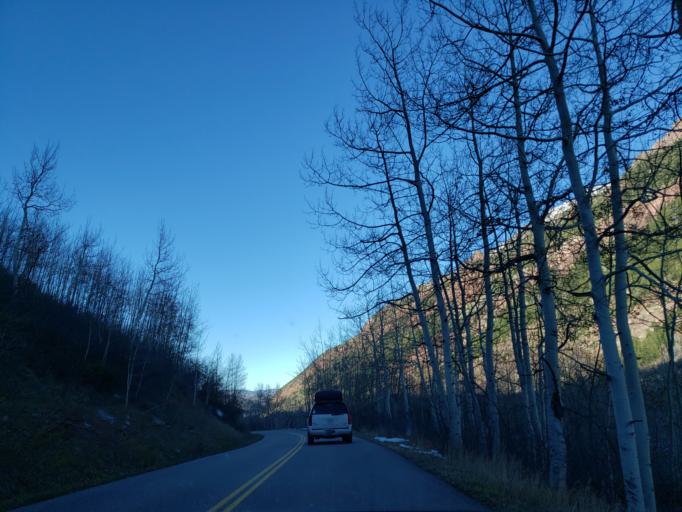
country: US
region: Colorado
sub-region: Pitkin County
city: Snowmass Village
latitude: 39.1198
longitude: -106.9093
